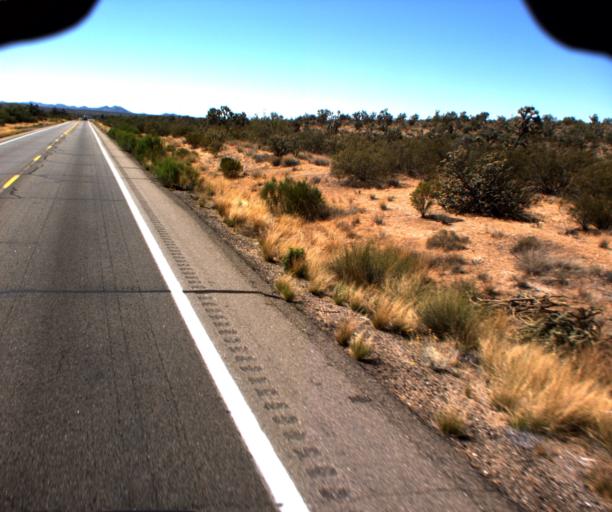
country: US
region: Arizona
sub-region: Yavapai County
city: Congress
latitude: 34.2389
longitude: -113.0752
